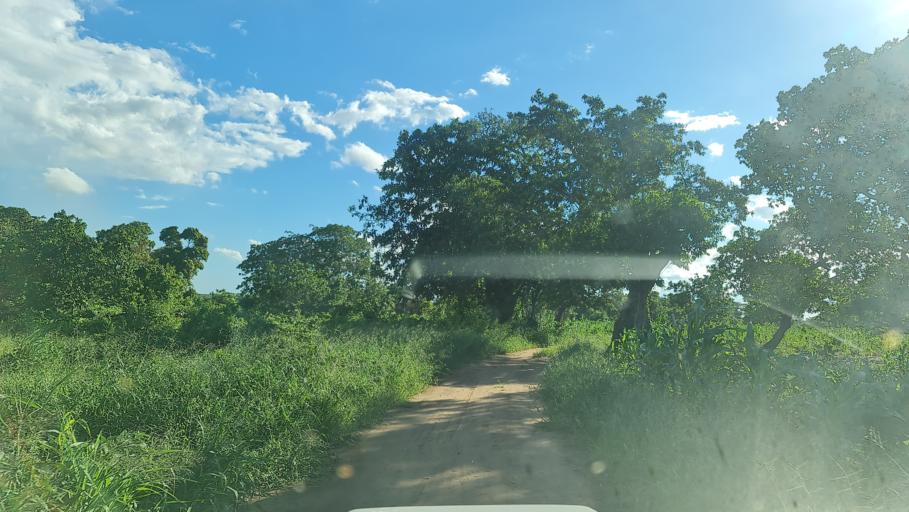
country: MZ
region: Nampula
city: Ilha de Mocambique
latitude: -14.9299
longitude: 40.2201
